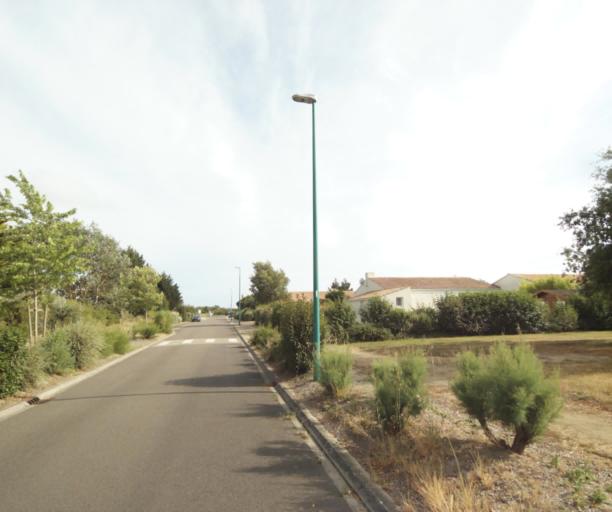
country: FR
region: Pays de la Loire
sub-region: Departement de la Vendee
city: Chateau-d'Olonne
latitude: 46.4875
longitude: -1.7334
